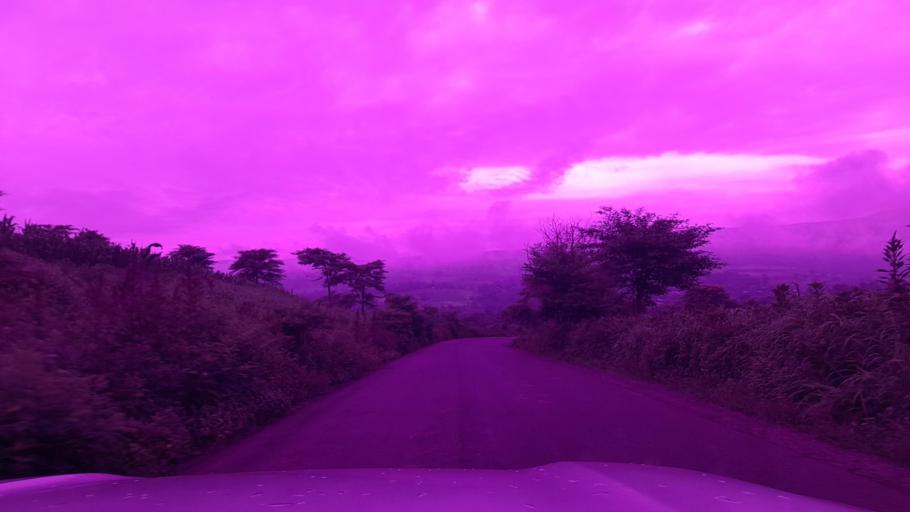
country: ET
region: Oromiya
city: Waliso
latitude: 8.2231
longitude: 37.5719
